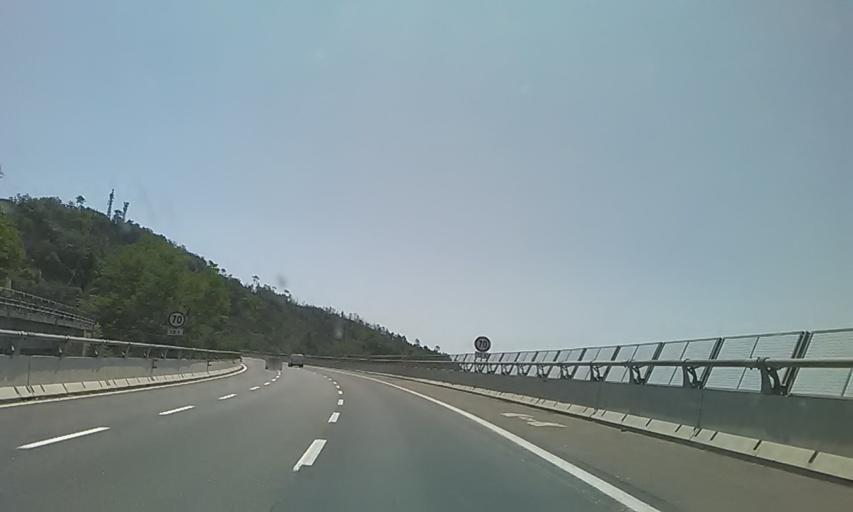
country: IT
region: Liguria
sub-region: Provincia di Genova
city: Mele
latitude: 44.4481
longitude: 8.7303
